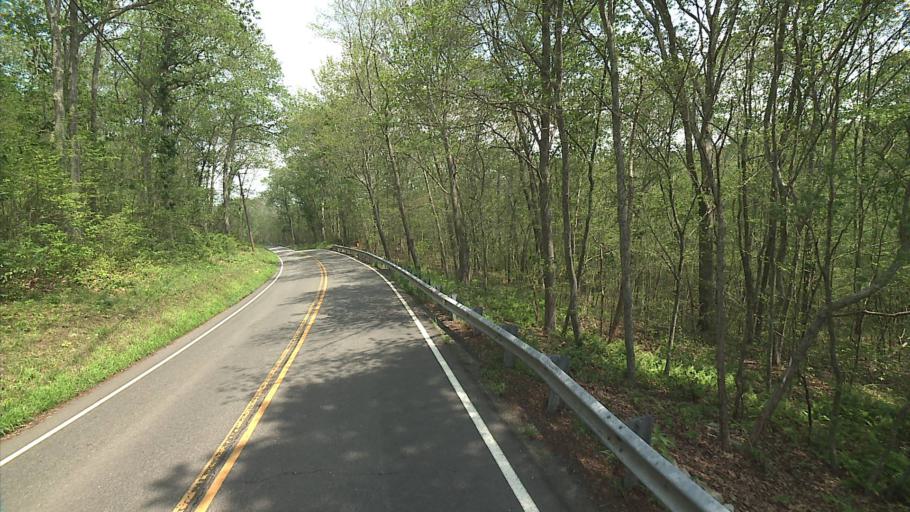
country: US
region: Connecticut
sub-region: Windham County
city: Moosup
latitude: 41.7500
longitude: -71.8528
